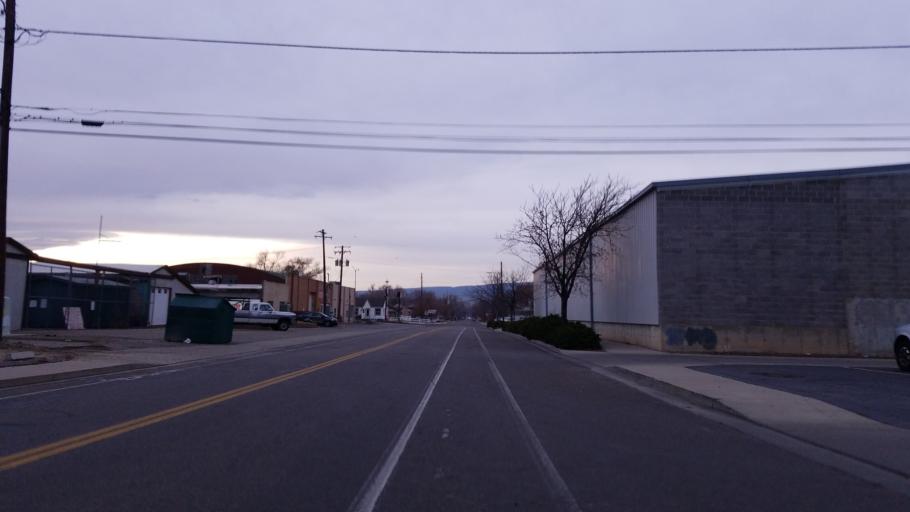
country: US
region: Colorado
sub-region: Mesa County
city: Grand Junction
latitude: 39.0788
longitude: -108.5679
